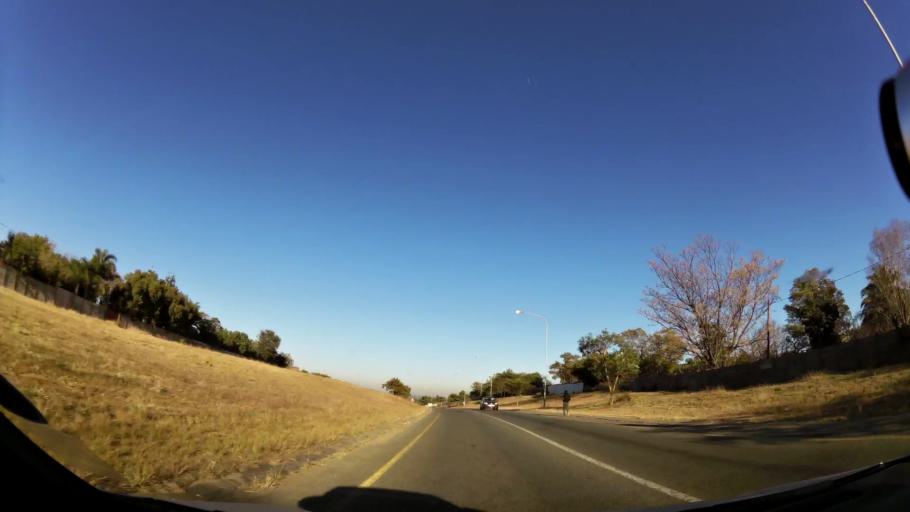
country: ZA
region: Gauteng
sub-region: City of Tshwane Metropolitan Municipality
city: Centurion
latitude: -25.9012
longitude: 28.1373
